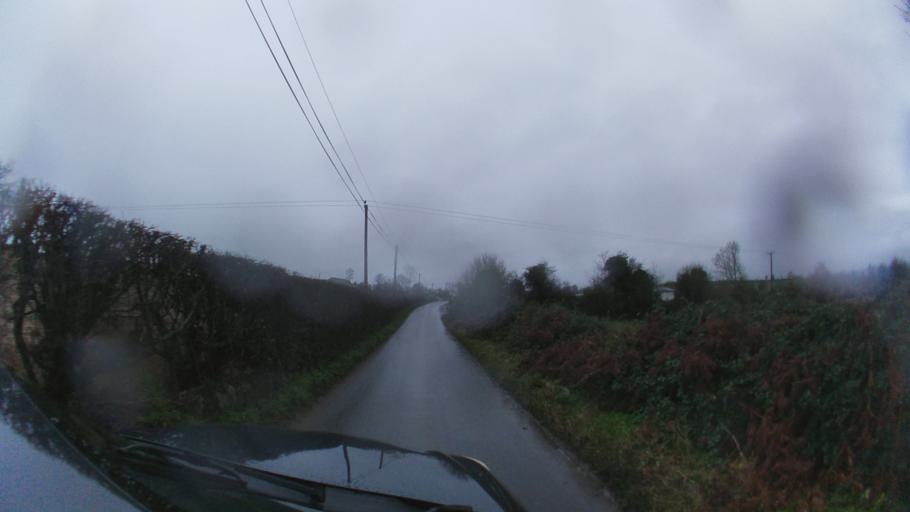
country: IE
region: Leinster
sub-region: Kilkenny
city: Graiguenamanagh
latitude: 52.5955
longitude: -6.9932
